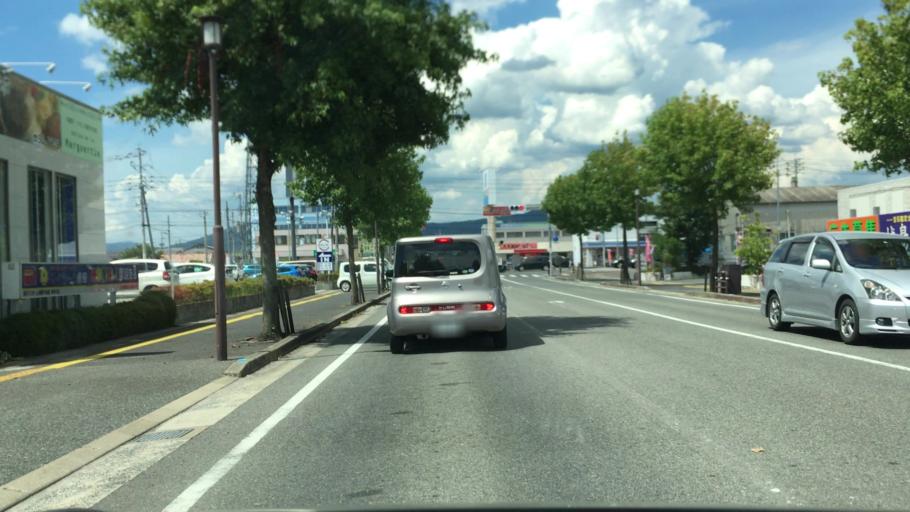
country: JP
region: Saga Prefecture
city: Saga-shi
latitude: 33.2755
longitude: 130.3052
